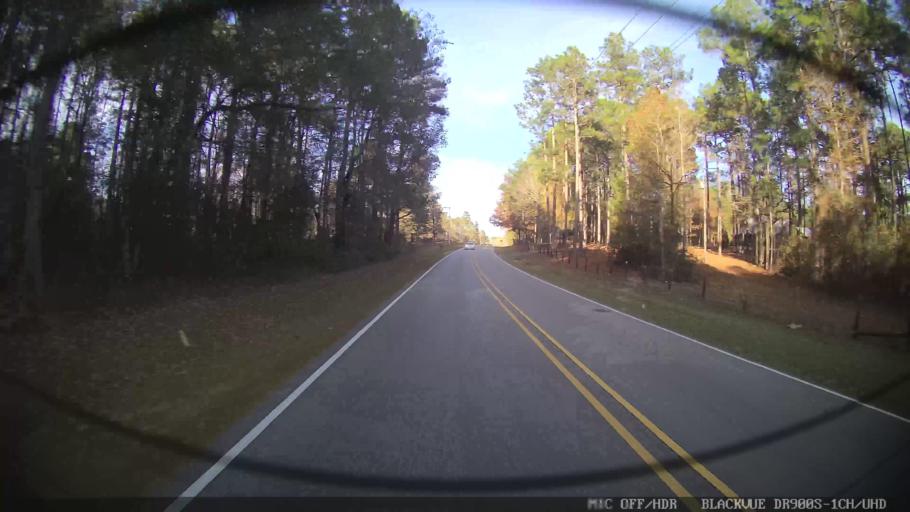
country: US
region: Mississippi
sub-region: Lamar County
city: Purvis
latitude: 31.1759
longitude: -89.2944
